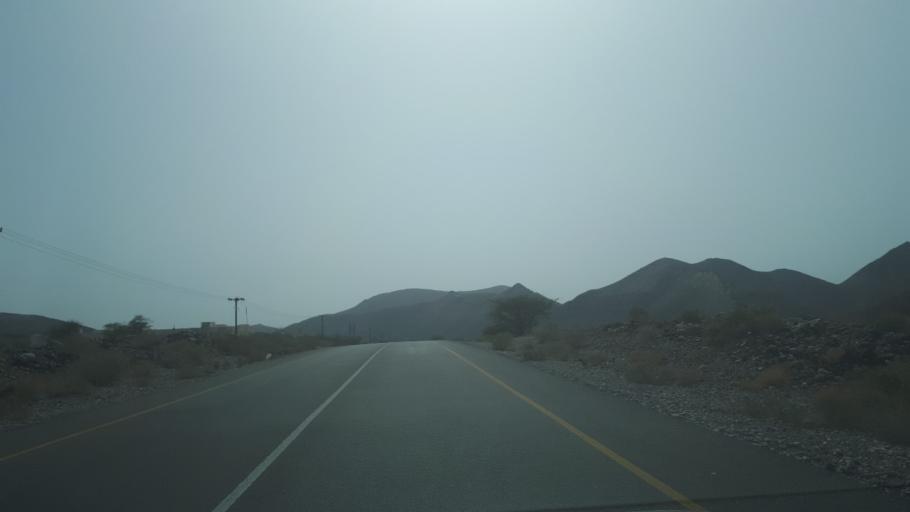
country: OM
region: Muhafazat ad Dakhiliyah
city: Bahla'
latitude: 23.2231
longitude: 56.9922
